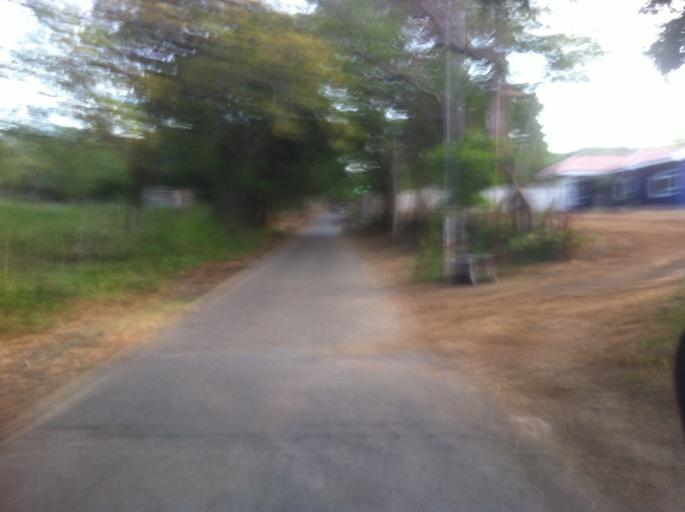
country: NI
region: Managua
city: Ciudad Sandino
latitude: 12.0921
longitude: -86.3340
